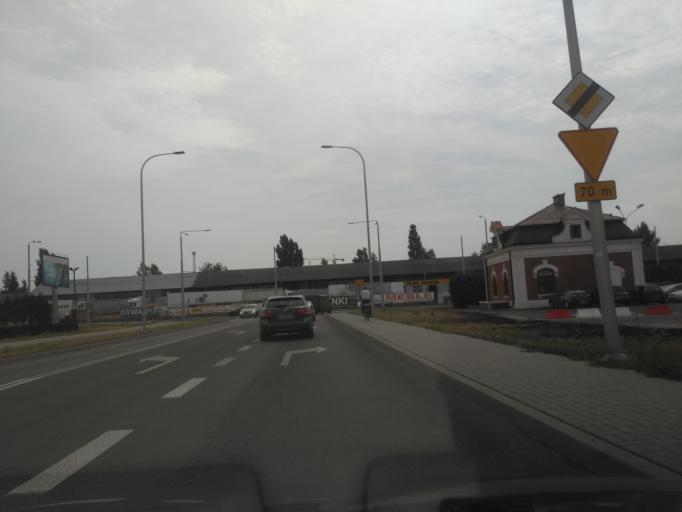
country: PL
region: Lublin Voivodeship
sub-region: Powiat lubelski
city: Lublin
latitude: 51.2289
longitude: 22.5571
